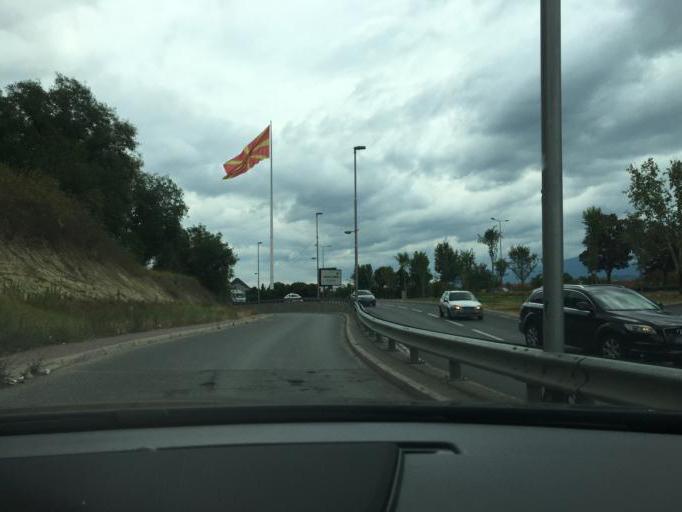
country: MK
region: Cair
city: Cair
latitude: 42.0002
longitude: 21.4488
